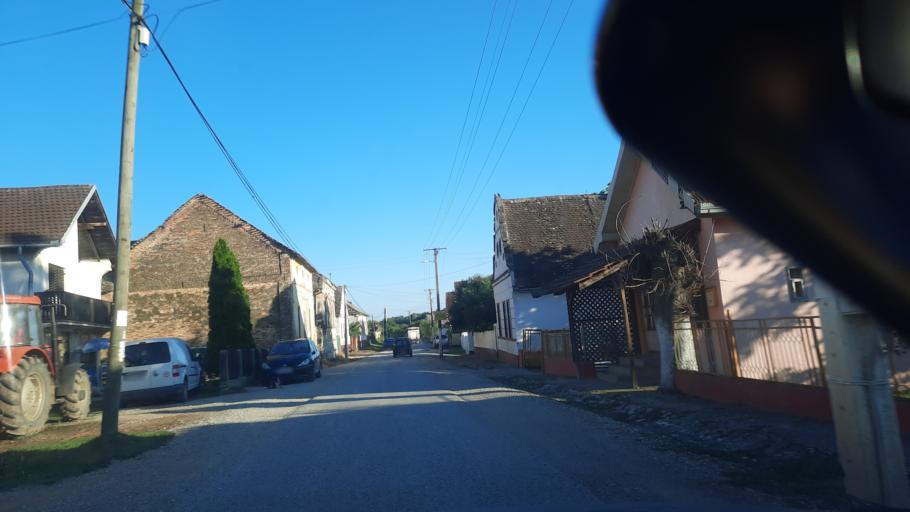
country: RS
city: Cortanovci
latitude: 45.1164
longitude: 19.9457
